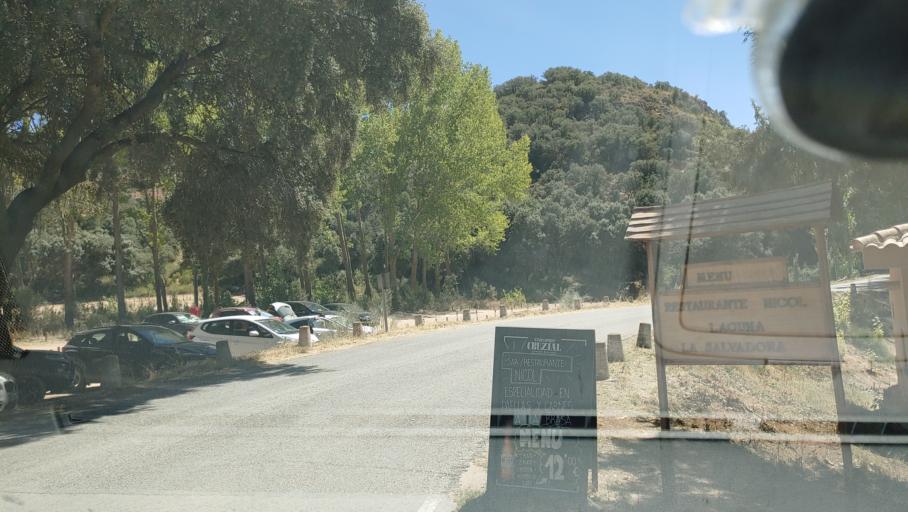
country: ES
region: Castille-La Mancha
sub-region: Provincia de Ciudad Real
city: Ruidera
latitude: 38.9506
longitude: -2.8553
